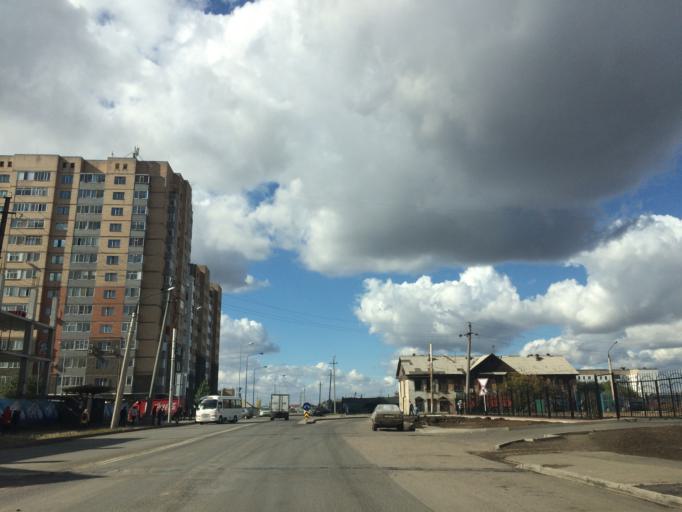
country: KZ
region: Astana Qalasy
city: Astana
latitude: 51.1976
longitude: 71.3881
